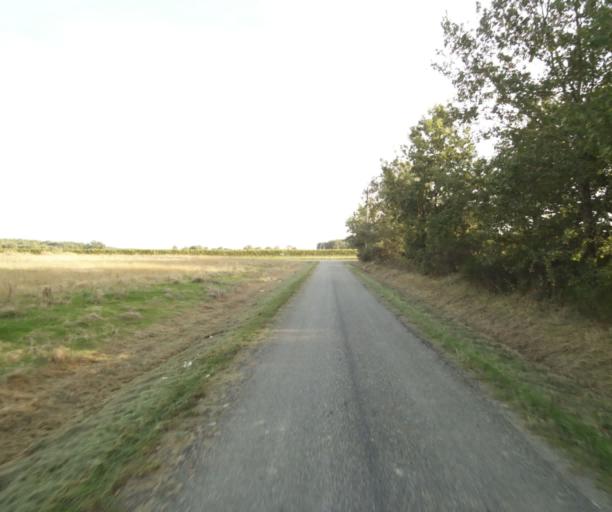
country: FR
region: Midi-Pyrenees
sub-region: Departement du Tarn-et-Garonne
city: Campsas
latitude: 43.8999
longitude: 1.3419
